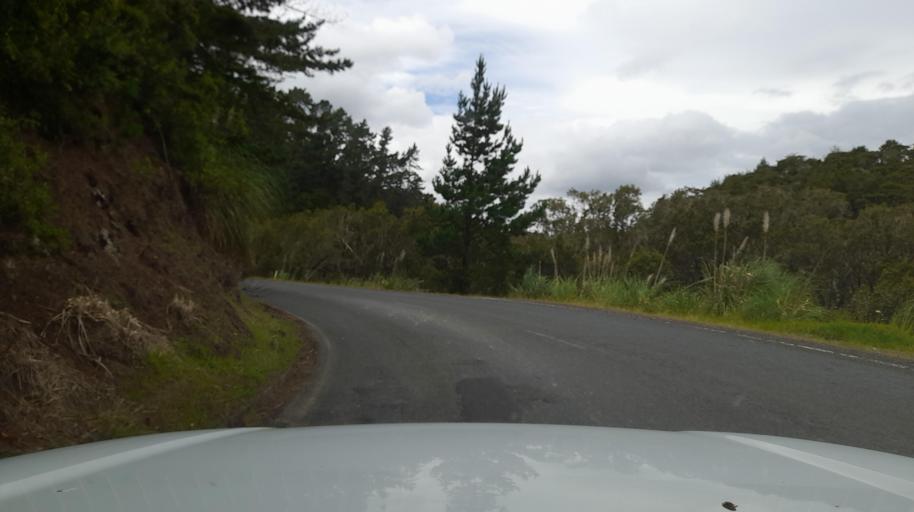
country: NZ
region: Northland
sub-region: Far North District
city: Kaitaia
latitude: -35.3637
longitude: 173.4727
